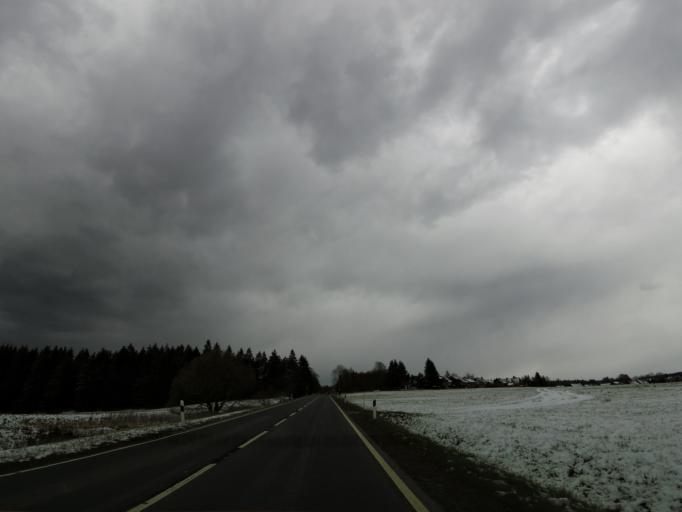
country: DE
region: Lower Saxony
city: Clausthal-Zellerfeld
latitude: 51.7741
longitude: 10.3223
